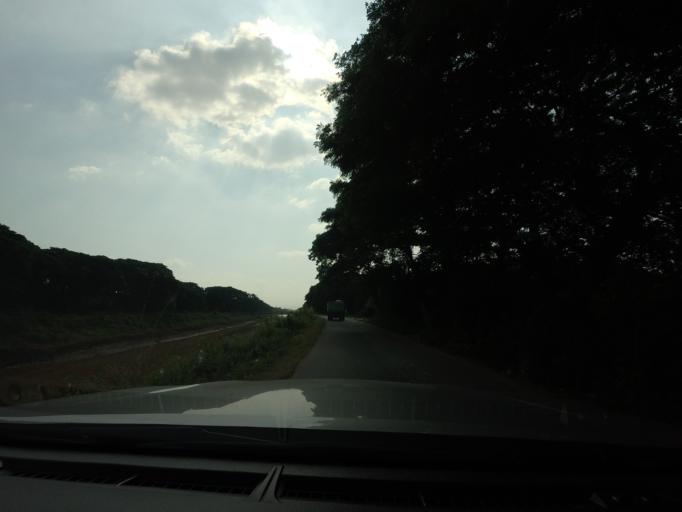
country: TH
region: Phitsanulok
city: Phitsanulok
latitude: 16.8047
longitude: 100.2136
